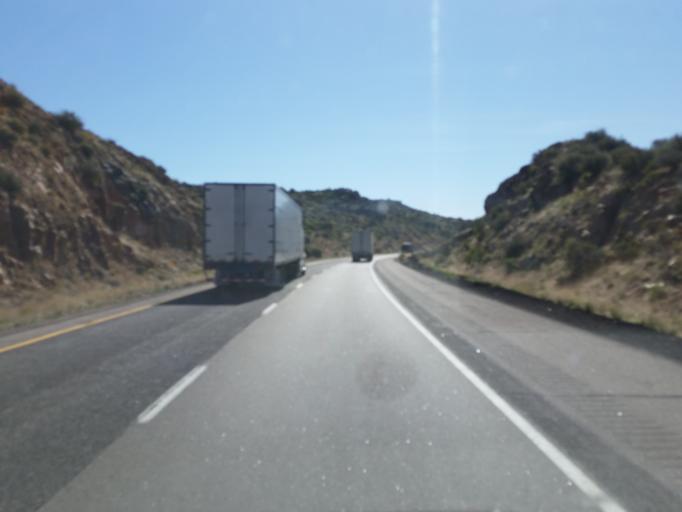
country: US
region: Arizona
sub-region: Mohave County
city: Peach Springs
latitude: 35.1772
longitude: -113.4882
